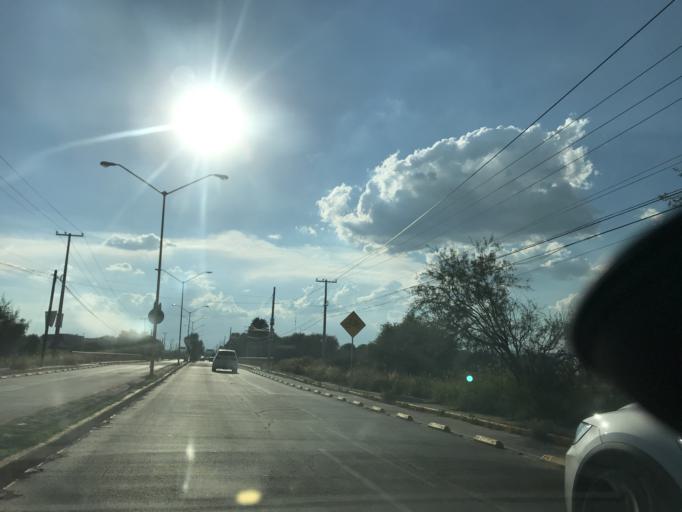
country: MX
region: Aguascalientes
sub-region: Aguascalientes
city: Pocitos
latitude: 21.9096
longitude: -102.3215
